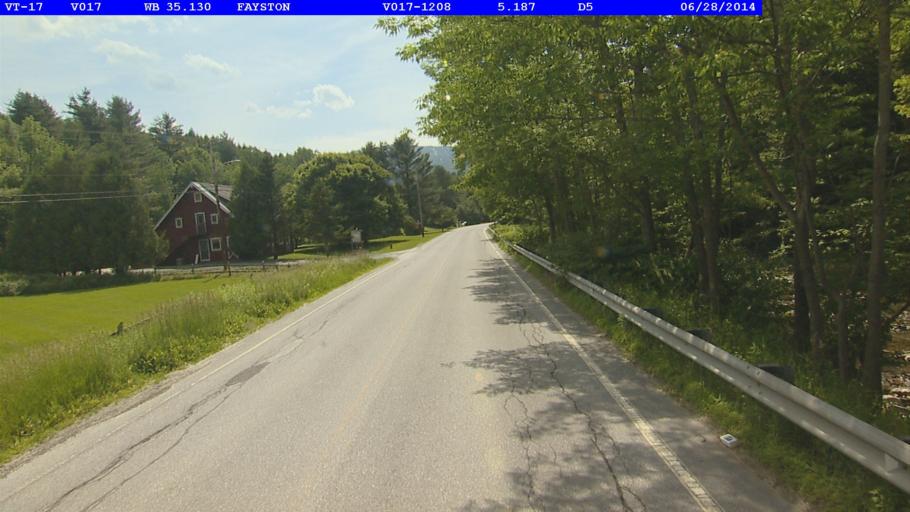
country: US
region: Vermont
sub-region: Washington County
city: Waterbury
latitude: 44.1829
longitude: -72.8554
